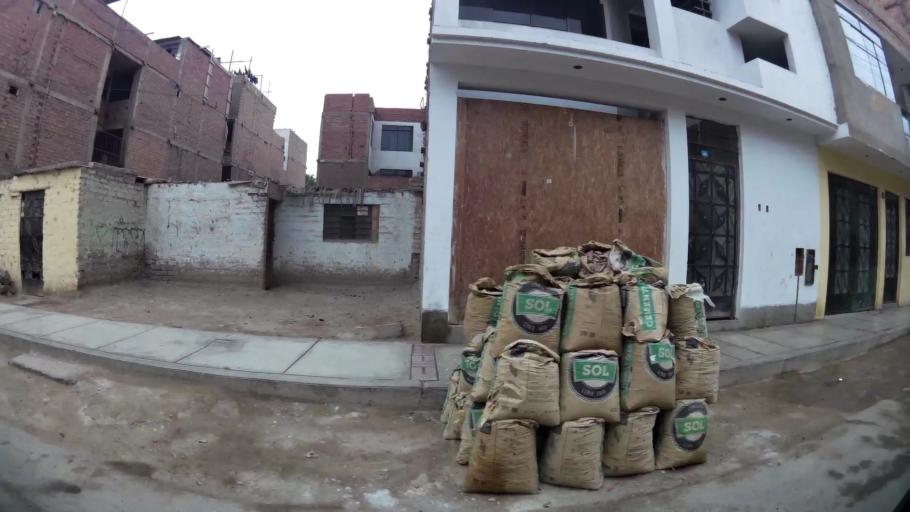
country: PE
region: Lima
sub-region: Lima
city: Independencia
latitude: -11.9662
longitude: -77.0779
